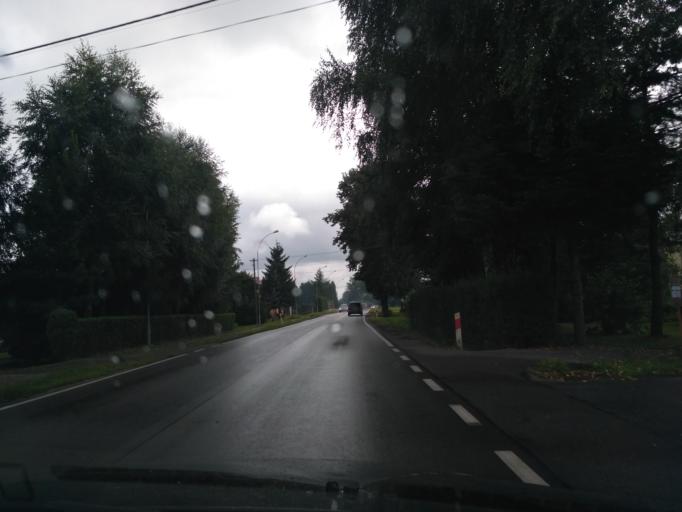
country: PL
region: Subcarpathian Voivodeship
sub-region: Powiat krosnienski
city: Korczyna
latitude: 49.7111
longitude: 21.7925
